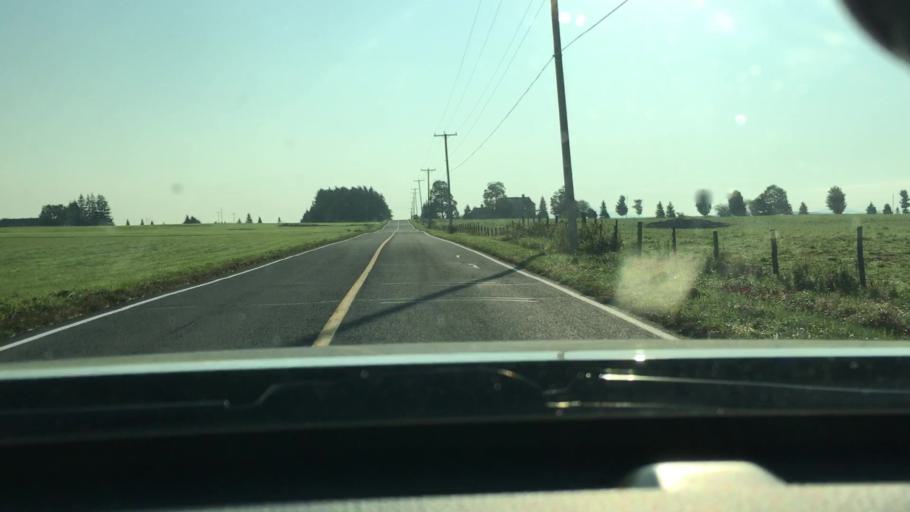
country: CA
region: Quebec
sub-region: Monteregie
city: Waterloo
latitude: 45.3557
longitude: -72.4955
